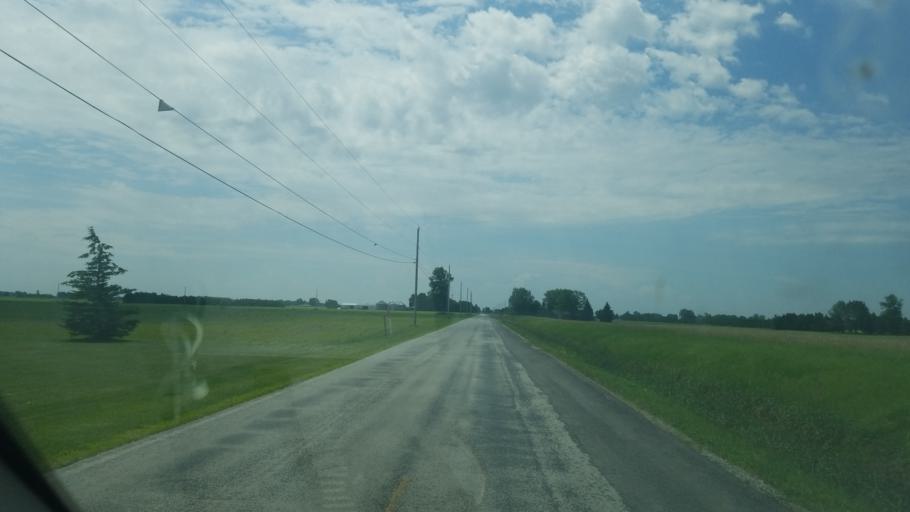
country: US
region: Ohio
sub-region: Wood County
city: Bowling Green
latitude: 41.2715
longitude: -83.5928
